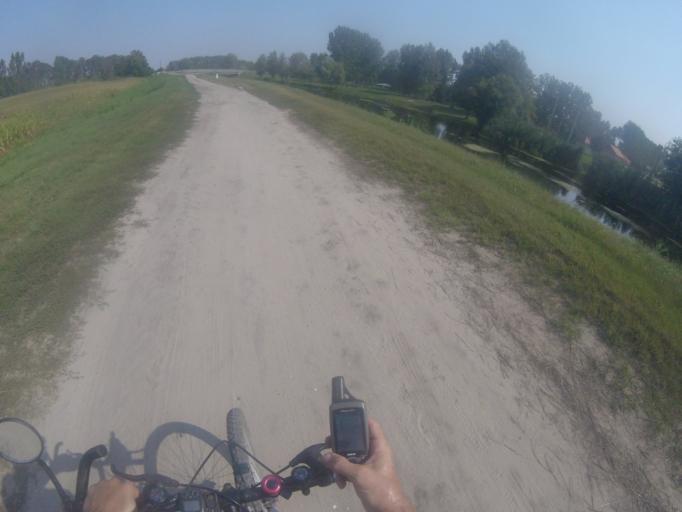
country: HU
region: Bacs-Kiskun
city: Ersekcsanad
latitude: 46.2509
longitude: 18.9705
